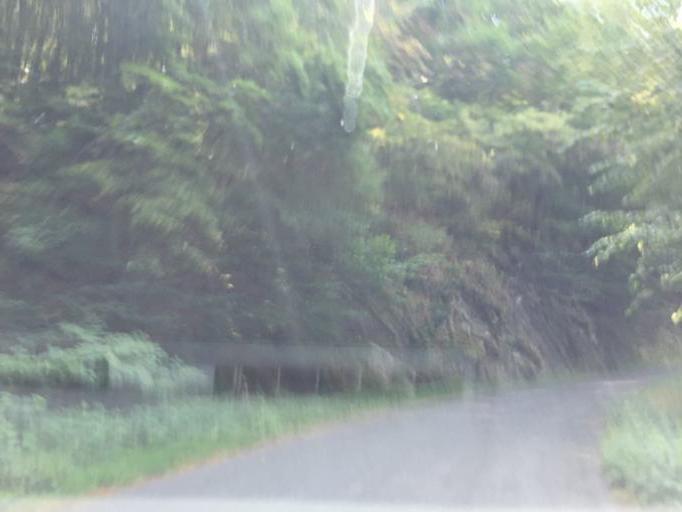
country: FR
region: Rhone-Alpes
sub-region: Departement de la Loire
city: Saint-Jean-Bonnefonds
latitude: 45.4177
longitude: 4.4502
